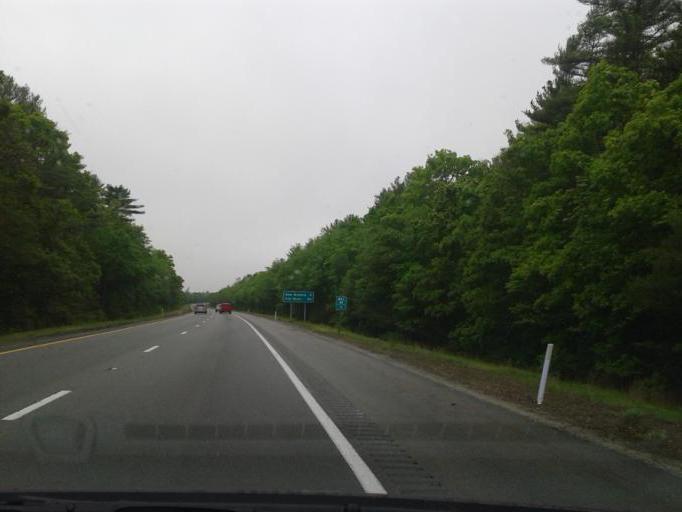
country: US
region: Massachusetts
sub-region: Plymouth County
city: Marion Center
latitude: 41.7191
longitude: -70.7829
